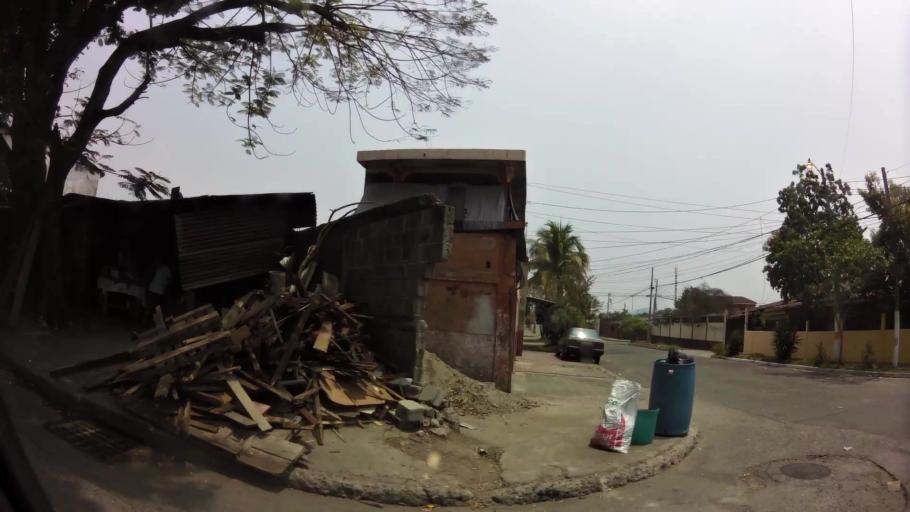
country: HN
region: Cortes
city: San Pedro Sula
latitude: 15.4988
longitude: -88.0112
